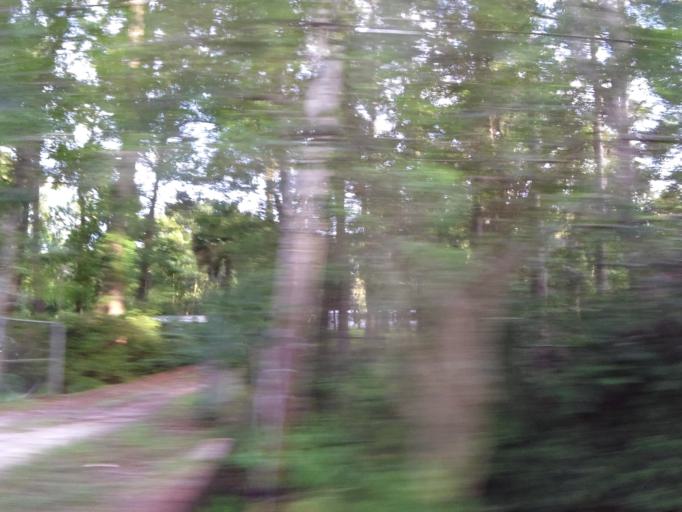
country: US
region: Florida
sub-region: Duval County
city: Jacksonville
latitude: 30.4164
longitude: -81.7076
